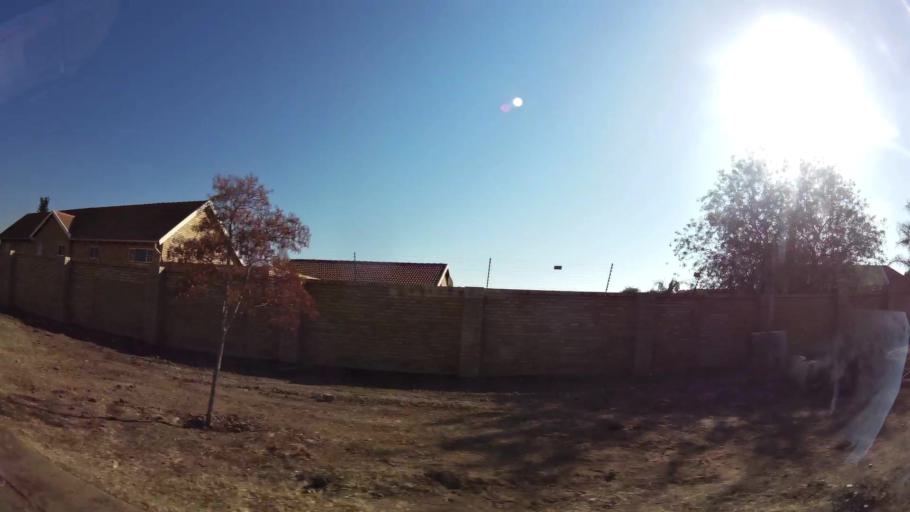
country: ZA
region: Gauteng
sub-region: City of Tshwane Metropolitan Municipality
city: Pretoria
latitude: -25.6724
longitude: 28.2315
